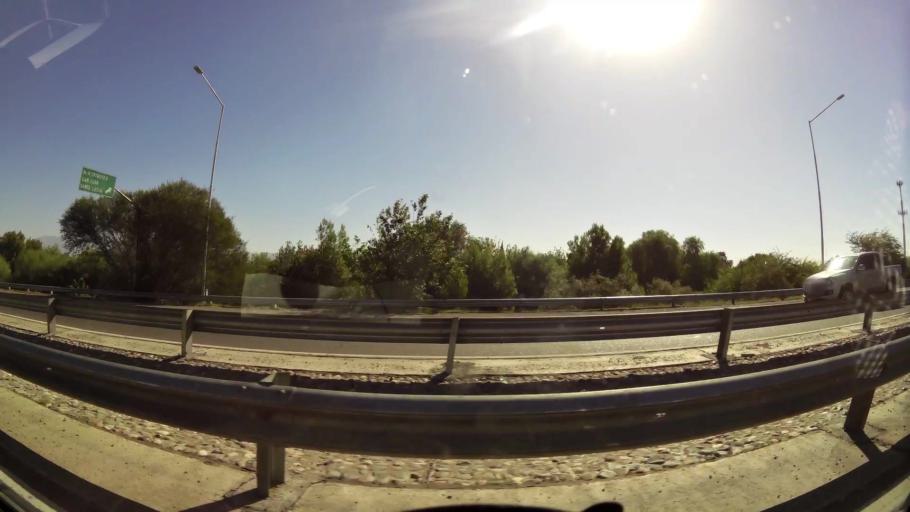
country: AR
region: San Juan
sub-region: Departamento de Santa Lucia
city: Santa Lucia
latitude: -31.5368
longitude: -68.5037
